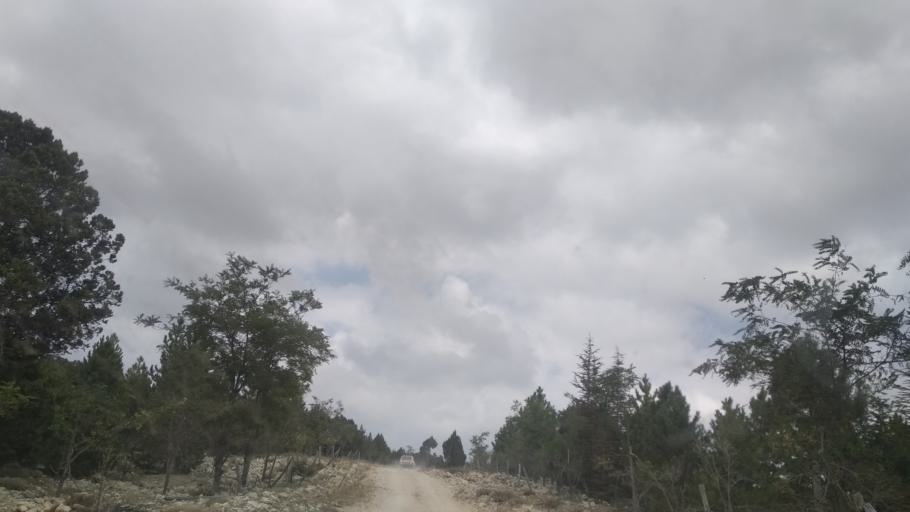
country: TR
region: Mersin
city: Sarikavak
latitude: 36.5719
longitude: 33.7625
